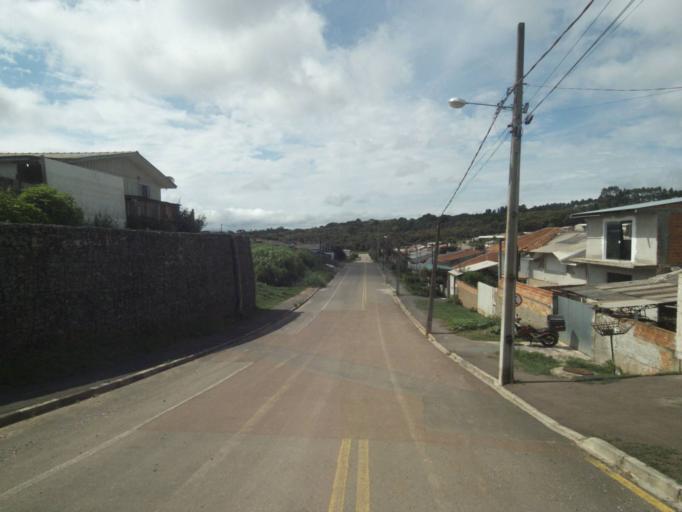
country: BR
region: Parana
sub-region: Campina Grande Do Sul
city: Campina Grande do Sul
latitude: -25.3345
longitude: -49.0679
